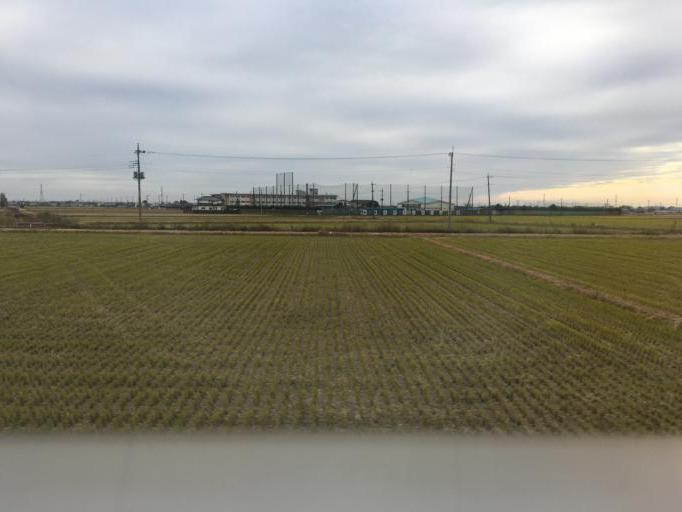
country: JP
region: Tochigi
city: Tochigi
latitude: 36.3561
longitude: 139.7711
